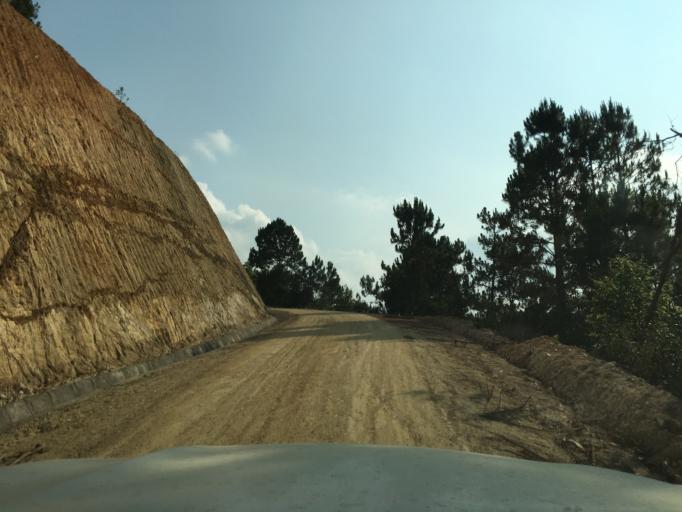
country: LA
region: Houaphan
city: Huameung
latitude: 20.1918
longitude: 103.8343
